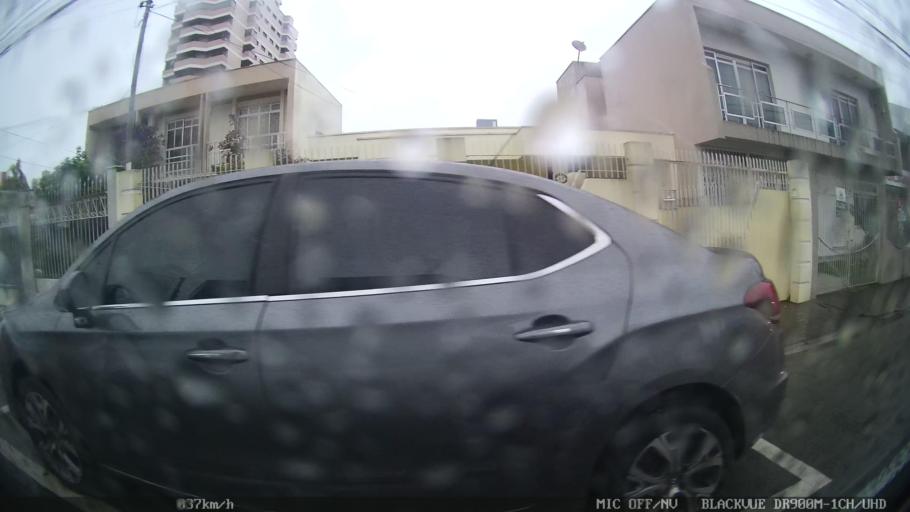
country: BR
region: Santa Catarina
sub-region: Itajai
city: Itajai
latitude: -26.9085
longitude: -48.6668
